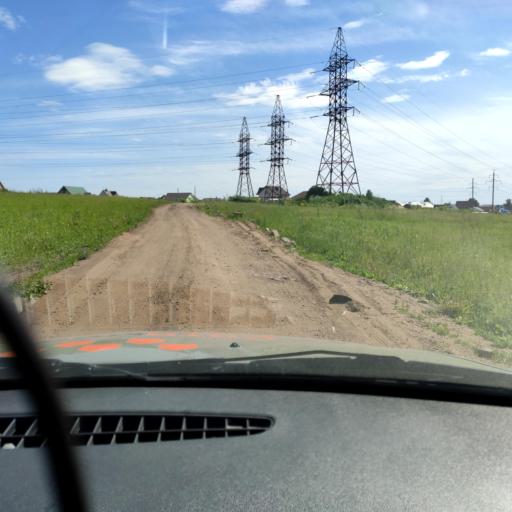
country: RU
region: Bashkortostan
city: Ufa
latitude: 54.6825
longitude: 56.0867
